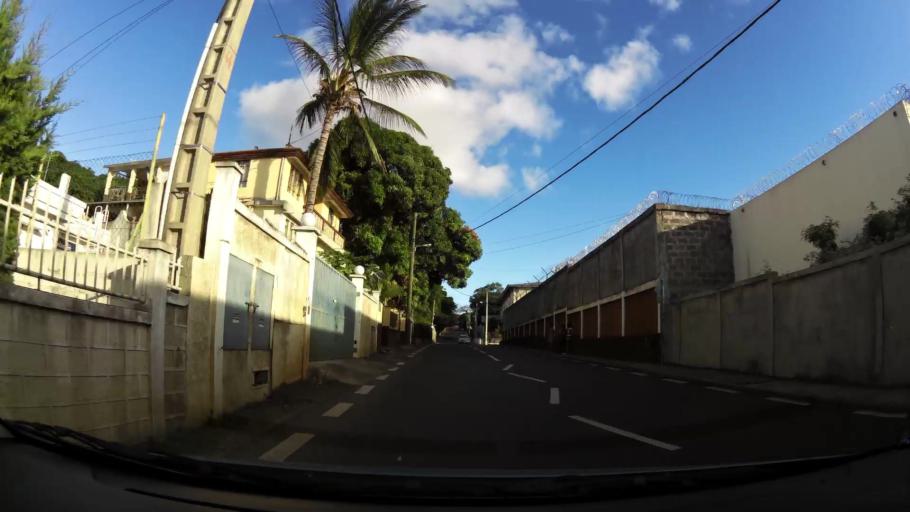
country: MU
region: Moka
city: Moka
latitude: -20.2248
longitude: 57.4636
